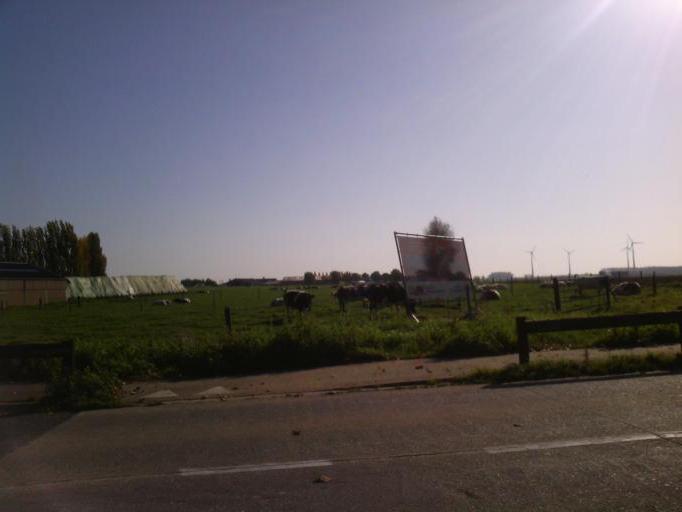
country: BE
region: Wallonia
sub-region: Province du Hainaut
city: Peruwelz
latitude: 50.5752
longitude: 3.6178
